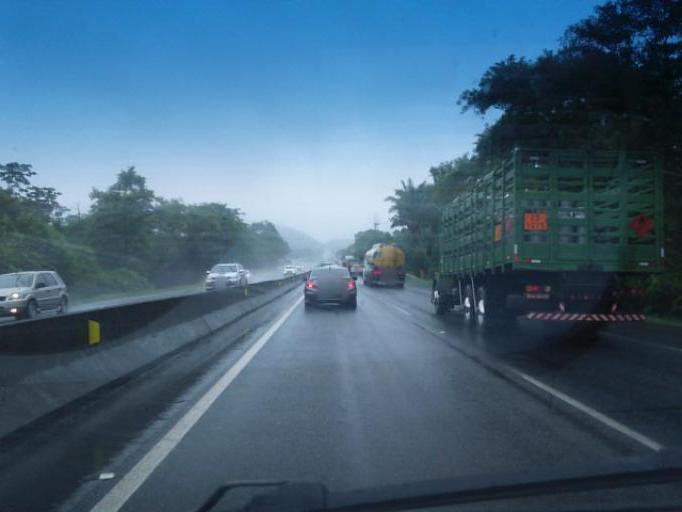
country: BR
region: Santa Catarina
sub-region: Joinville
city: Joinville
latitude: -26.1100
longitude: -48.8739
